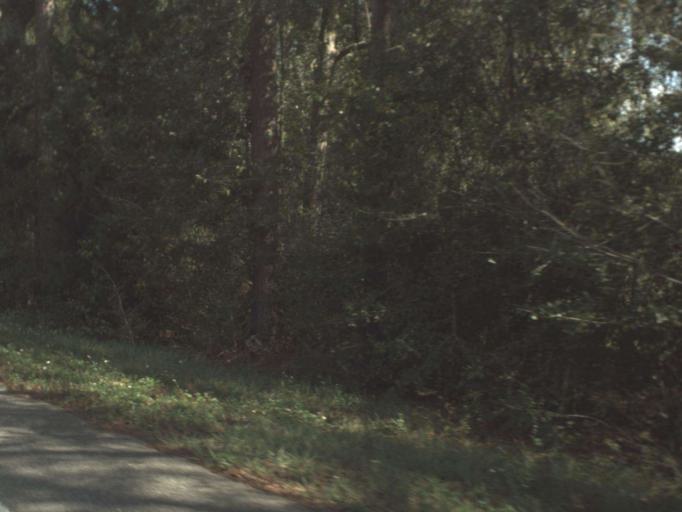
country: US
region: Alabama
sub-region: Geneva County
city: Samson
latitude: 30.9661
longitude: -86.1362
